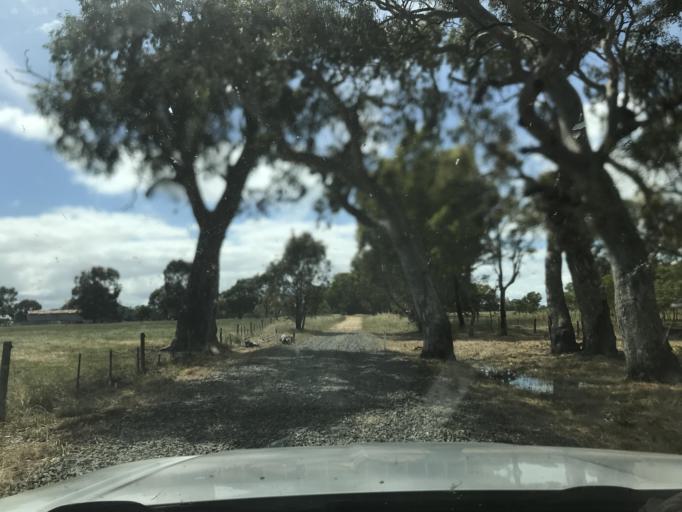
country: AU
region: South Australia
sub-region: Naracoorte and Lucindale
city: Naracoorte
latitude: -37.0190
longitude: 141.0980
